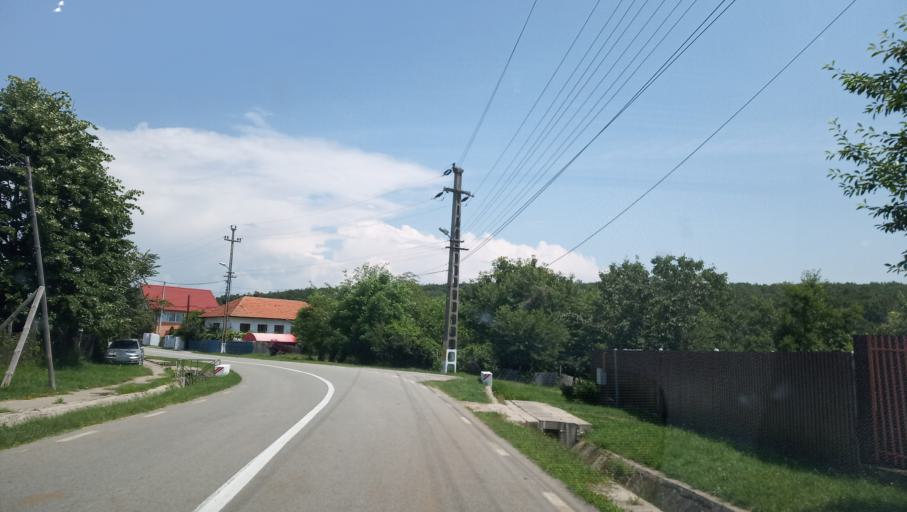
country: RO
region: Gorj
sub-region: Comuna Turcinesti
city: Turcinesti
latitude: 45.0475
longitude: 23.3457
